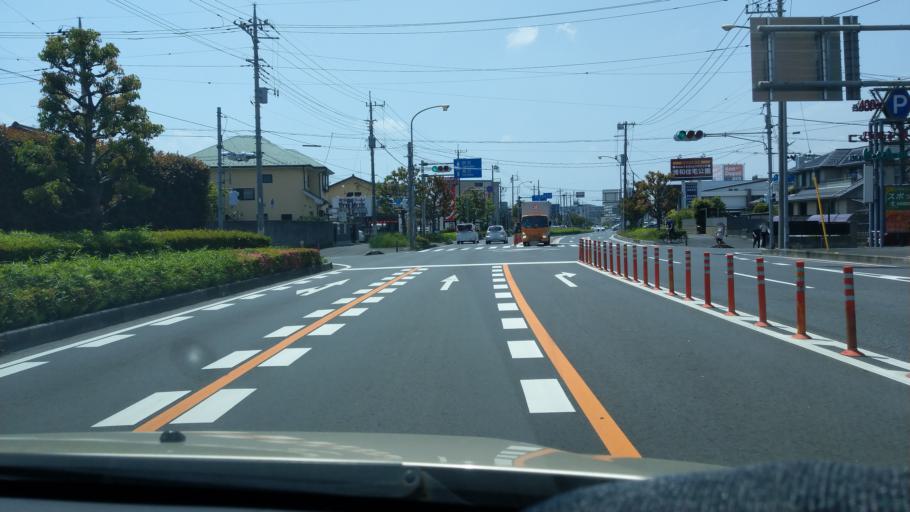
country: JP
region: Saitama
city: Saitama
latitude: 35.8740
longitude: 139.6790
